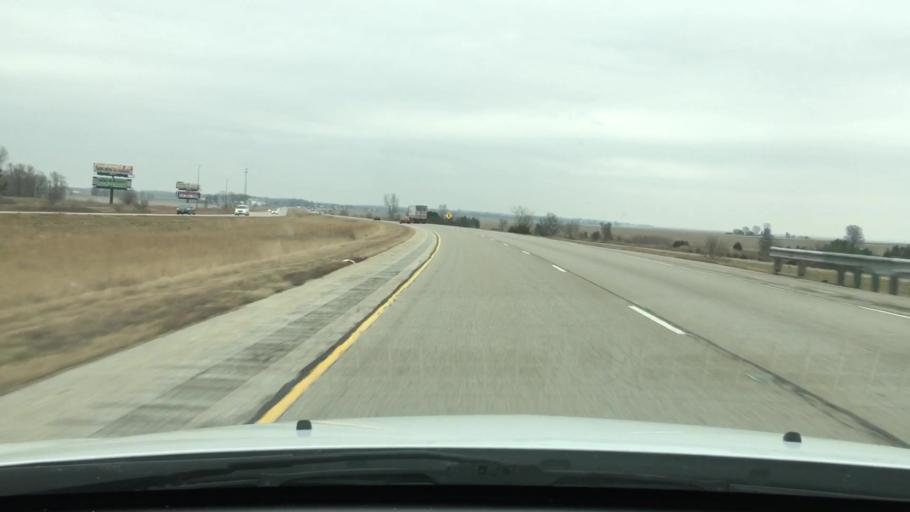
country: US
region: Illinois
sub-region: Logan County
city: Atlanta
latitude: 40.3127
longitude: -89.1618
